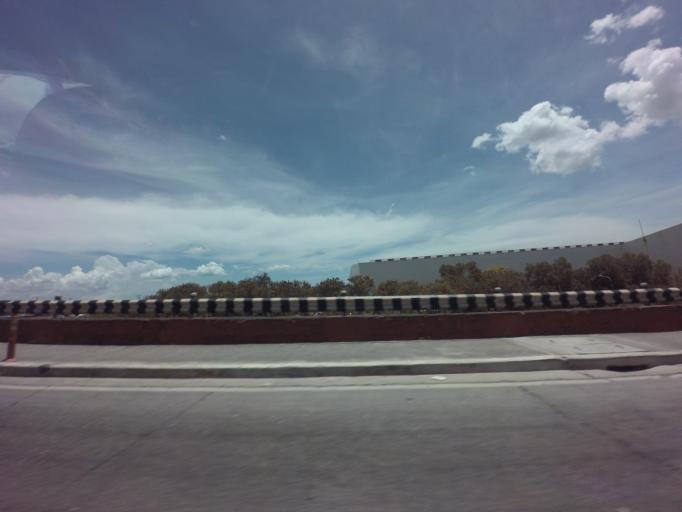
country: PH
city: Sambayanihan People's Village
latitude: 14.4935
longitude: 120.9962
